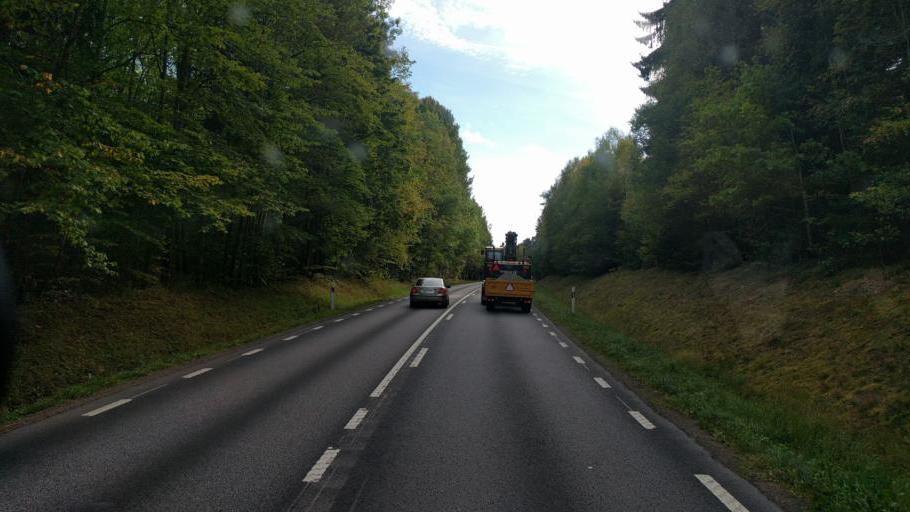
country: SE
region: OEstergoetland
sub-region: Kinda Kommun
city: Kisa
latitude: 57.9684
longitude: 15.6530
